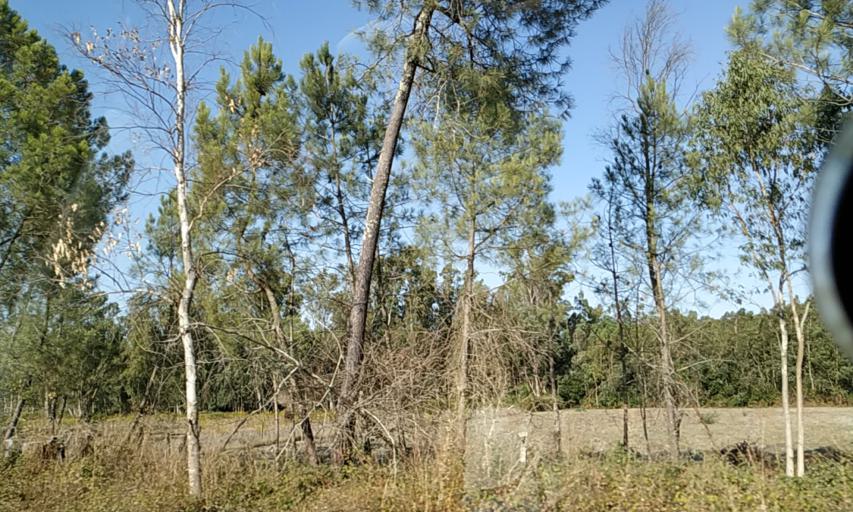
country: PT
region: Santarem
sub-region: Coruche
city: Coruche
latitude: 39.0052
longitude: -8.5608
